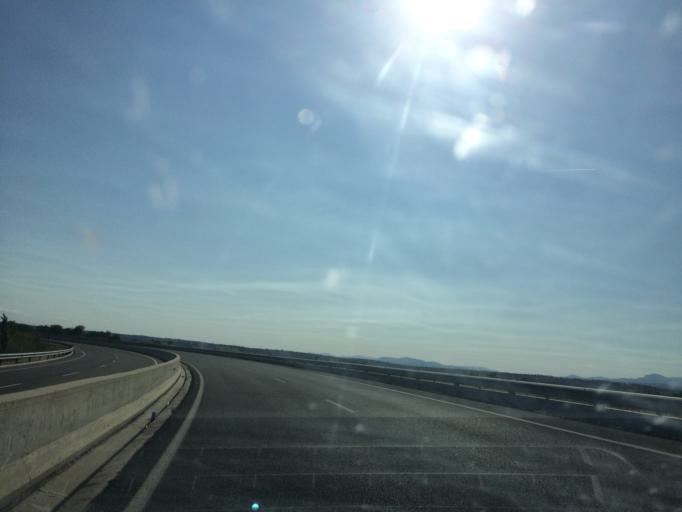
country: ES
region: Madrid
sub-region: Provincia de Madrid
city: Fuente el Saz
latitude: 40.6508
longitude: -3.5150
